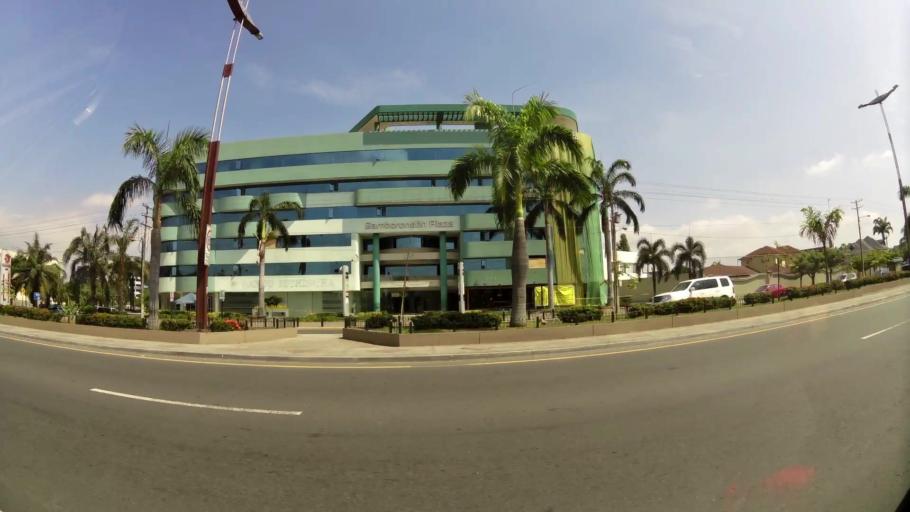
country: EC
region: Guayas
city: Eloy Alfaro
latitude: -2.1374
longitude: -79.8634
